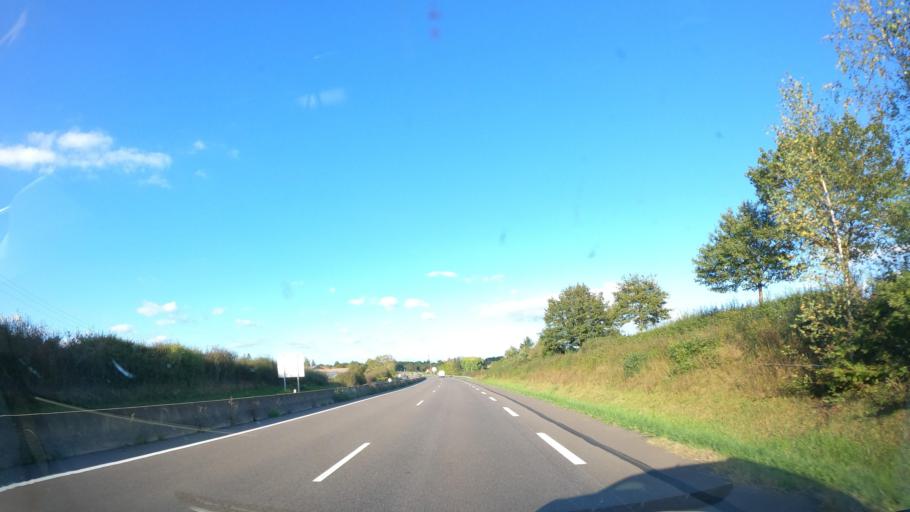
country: FR
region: Bourgogne
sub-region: Departement de Saone-et-Loire
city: Ciry-le-Noble
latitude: 46.6379
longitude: 4.3267
